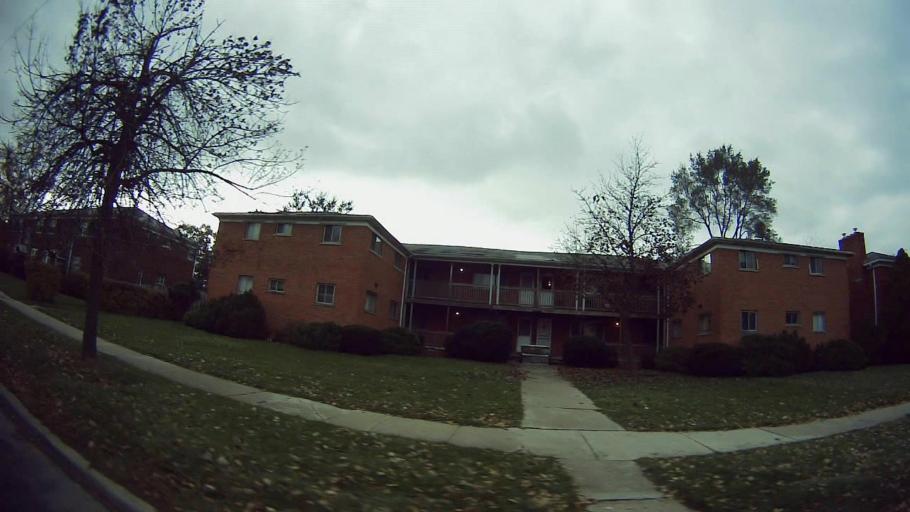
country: US
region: Michigan
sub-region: Macomb County
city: Warren
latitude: 42.4296
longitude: -83.0045
